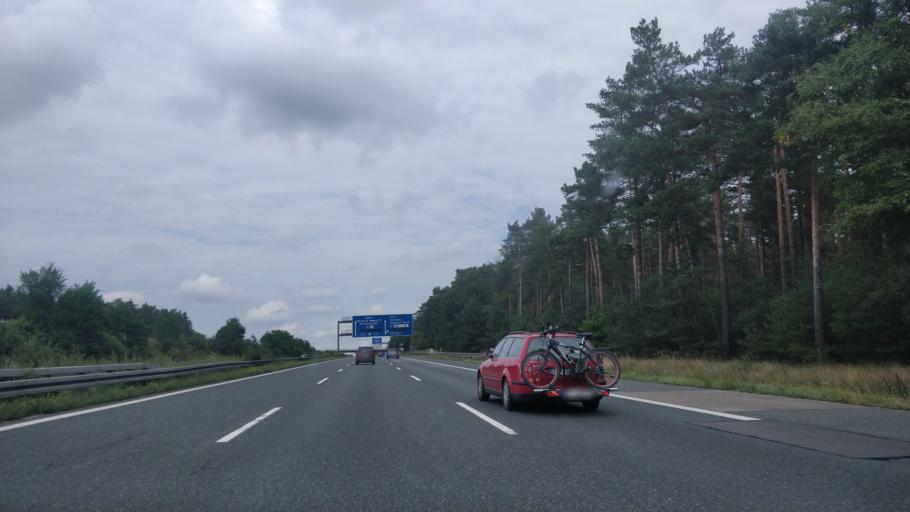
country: DE
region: Bavaria
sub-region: Regierungsbezirk Mittelfranken
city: Feucht
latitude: 49.3335
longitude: 11.2038
